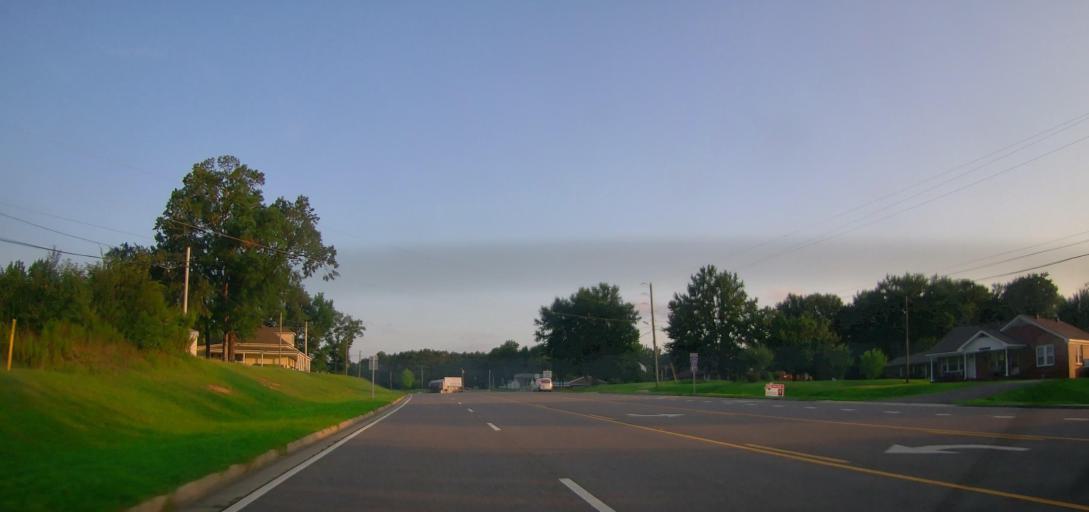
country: US
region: Alabama
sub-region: Marion County
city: Hamilton
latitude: 34.1013
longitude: -87.9889
